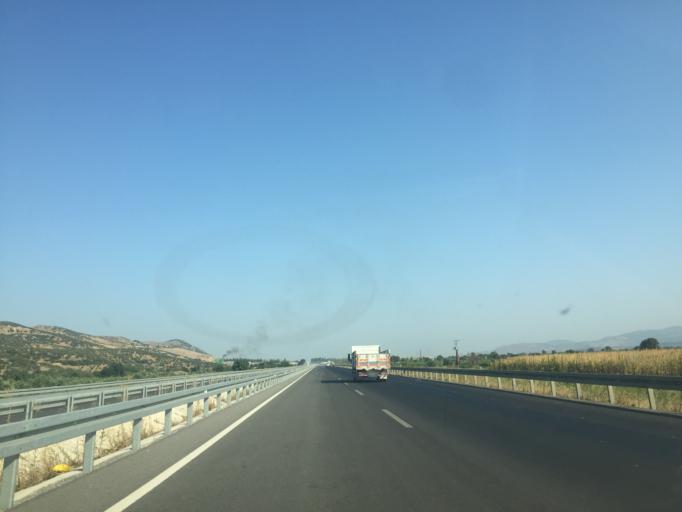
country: TR
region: Manisa
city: Golmarmara
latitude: 38.6844
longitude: 27.9407
